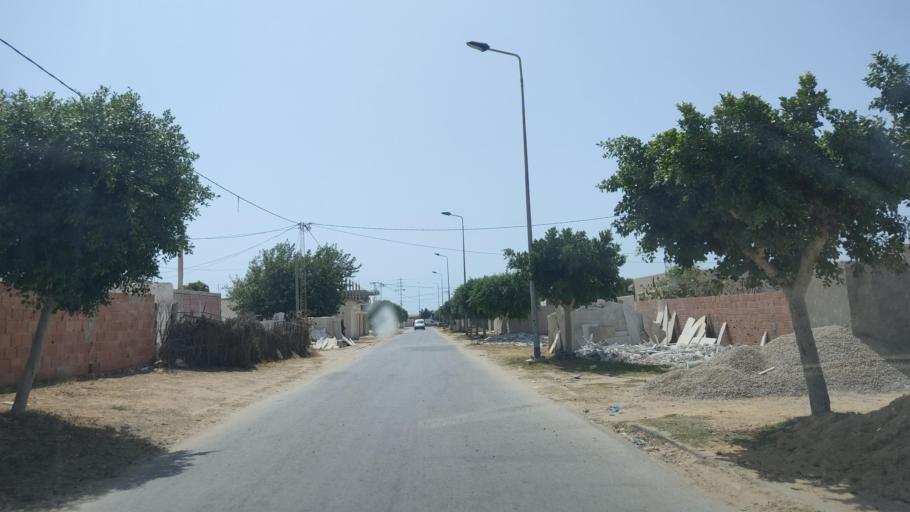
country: TN
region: Safaqis
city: Sfax
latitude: 34.6676
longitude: 10.7084
